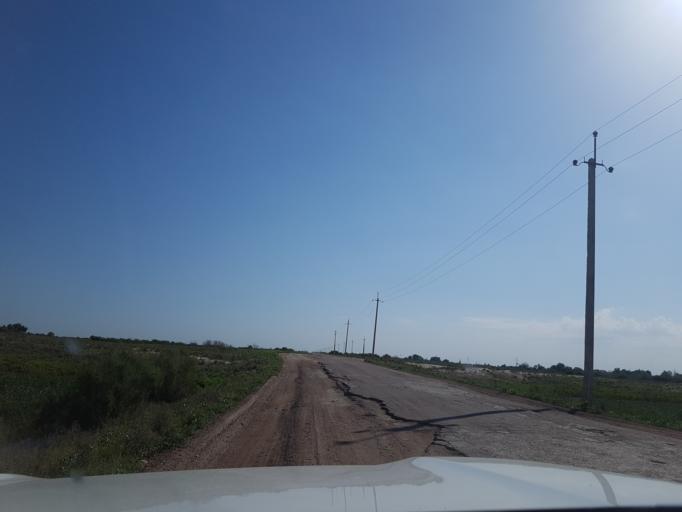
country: TM
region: Dasoguz
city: Koeneuergench
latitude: 42.0542
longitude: 58.8357
